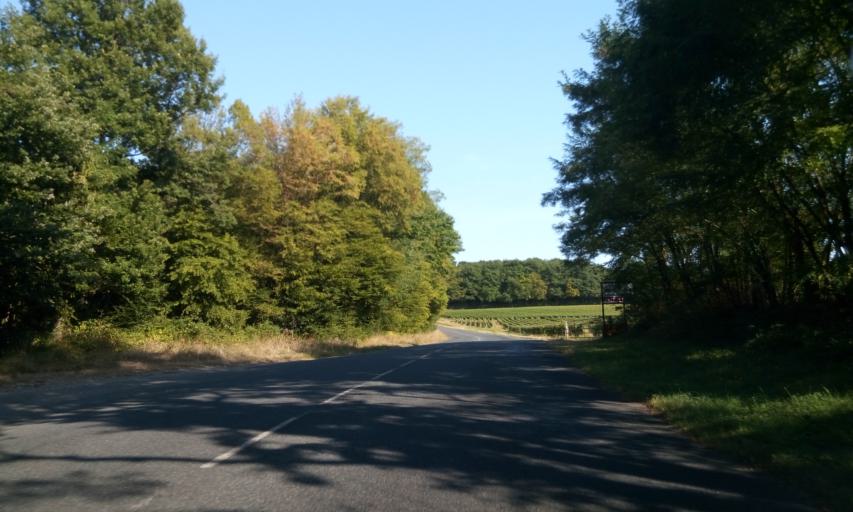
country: FR
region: Rhone-Alpes
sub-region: Departement du Rhone
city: Charnay
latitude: 45.9271
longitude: 4.6607
